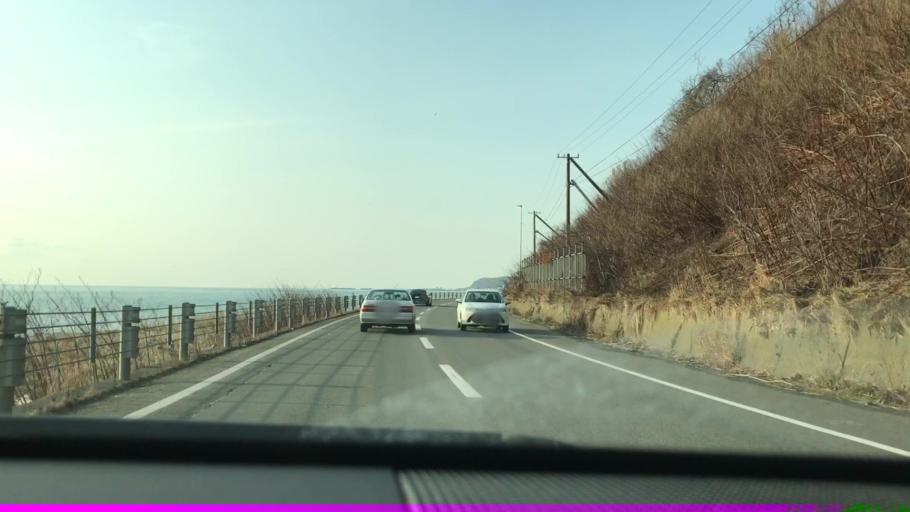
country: JP
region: Hokkaido
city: Shizunai-furukawacho
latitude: 42.2330
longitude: 142.6039
